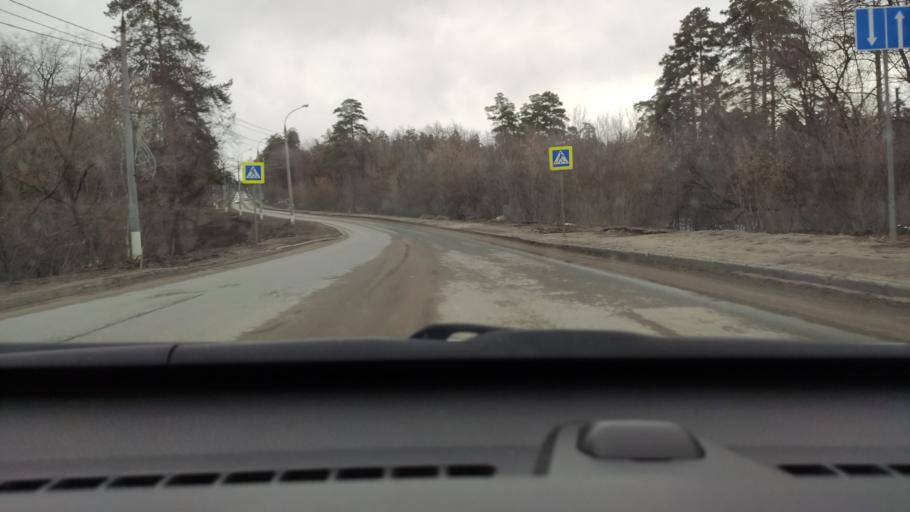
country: RU
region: Samara
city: Tol'yatti
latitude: 53.4952
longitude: 49.2916
